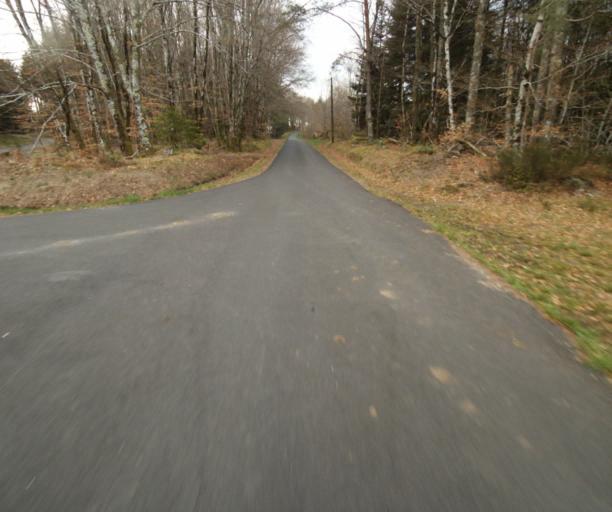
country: FR
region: Limousin
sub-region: Departement de la Correze
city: Argentat
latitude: 45.2182
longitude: 1.9570
